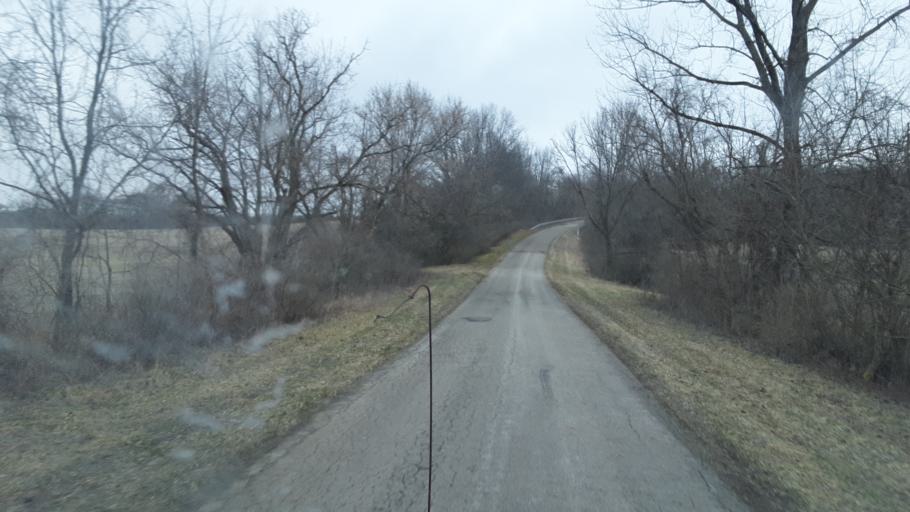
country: US
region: Ohio
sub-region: Perry County
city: Thornport
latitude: 39.9376
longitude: -82.3606
